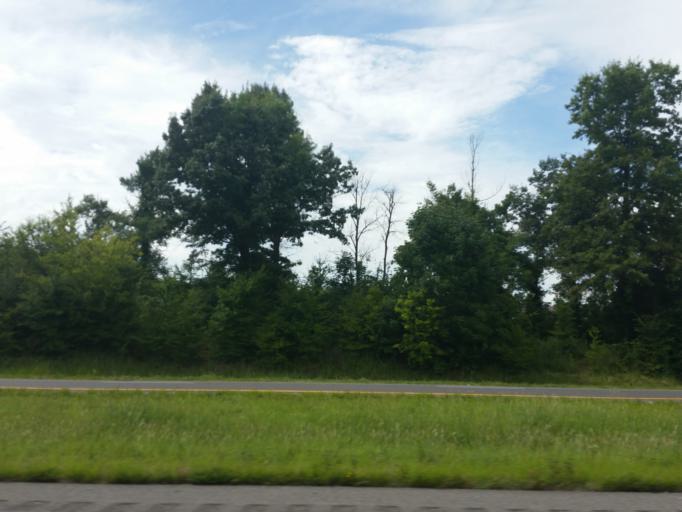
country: US
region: Kentucky
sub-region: Marshall County
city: Calvert City
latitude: 37.0072
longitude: -88.3207
